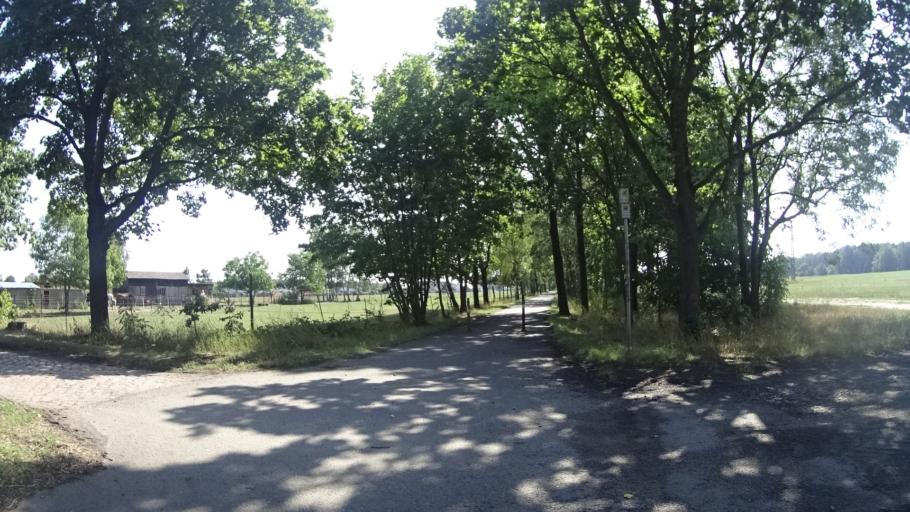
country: DE
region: Brandenburg
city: Cottbus
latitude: 51.7957
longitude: 14.2977
